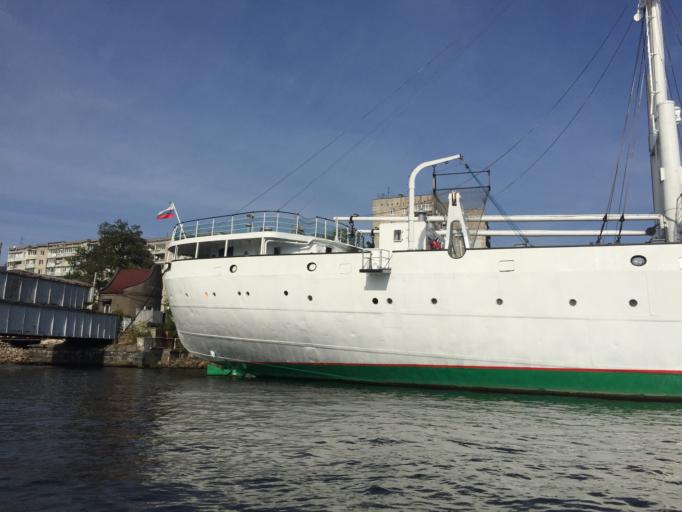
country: RU
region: Kaliningrad
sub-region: Gorod Kaliningrad
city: Kaliningrad
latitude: 54.7060
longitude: 20.4992
